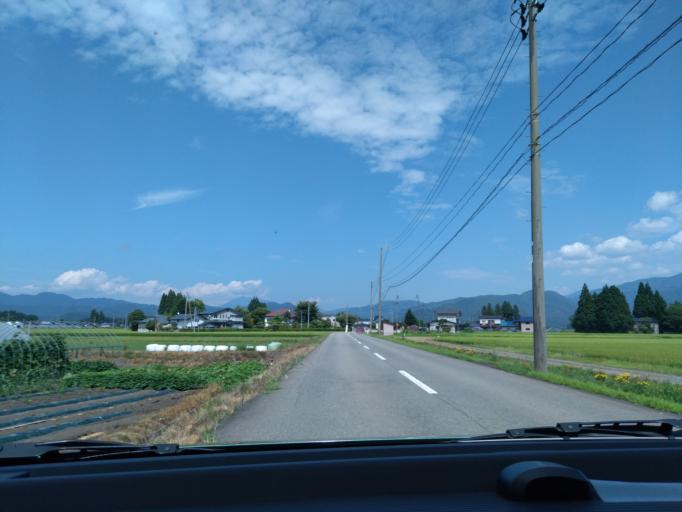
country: JP
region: Akita
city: Kakunodatemachi
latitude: 39.6040
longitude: 140.5888
